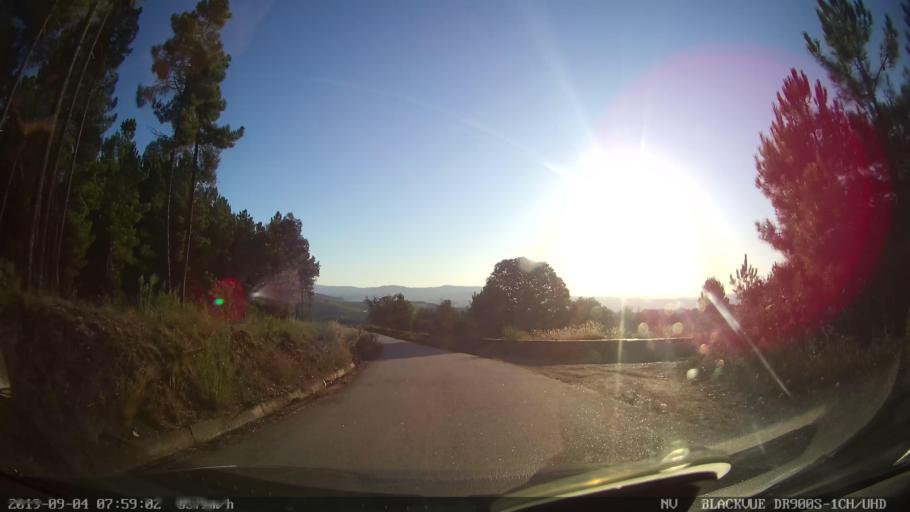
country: PT
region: Vila Real
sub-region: Sabrosa
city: Sabrosa
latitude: 41.2496
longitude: -7.5947
